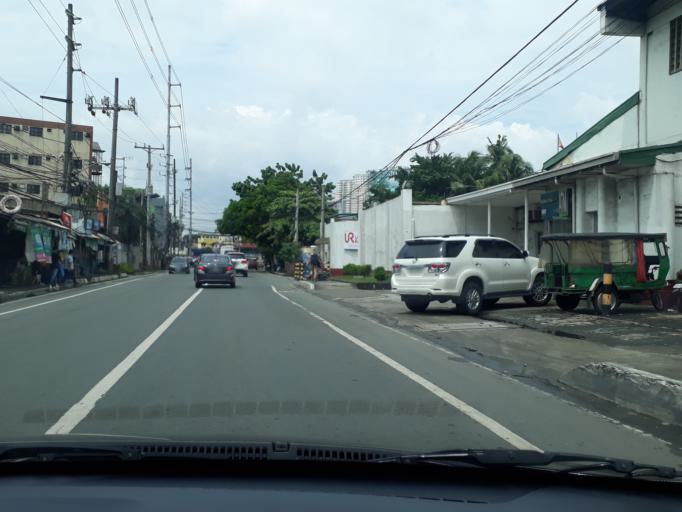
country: PH
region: Metro Manila
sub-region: Pasig
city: Pasig City
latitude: 14.5925
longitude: 121.0869
